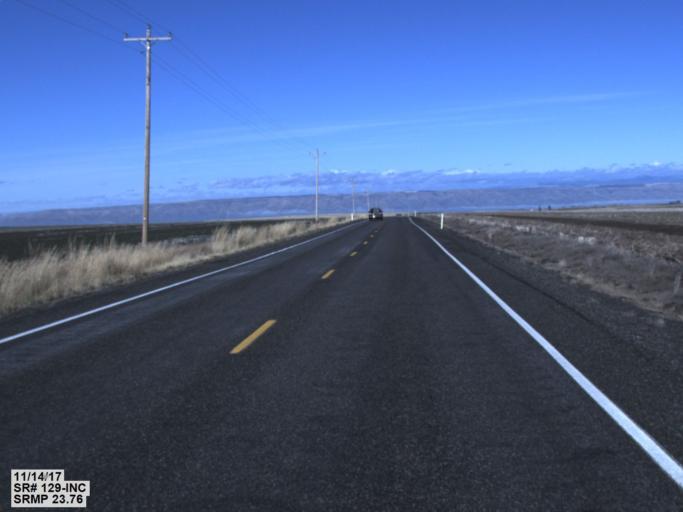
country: US
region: Washington
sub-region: Asotin County
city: Asotin
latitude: 46.2092
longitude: -117.0703
